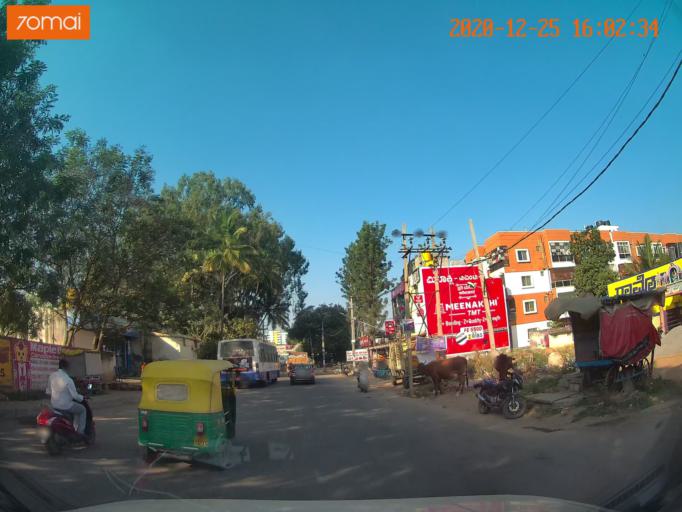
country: IN
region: Karnataka
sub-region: Bangalore Urban
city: Bangalore
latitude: 12.8823
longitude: 77.6247
